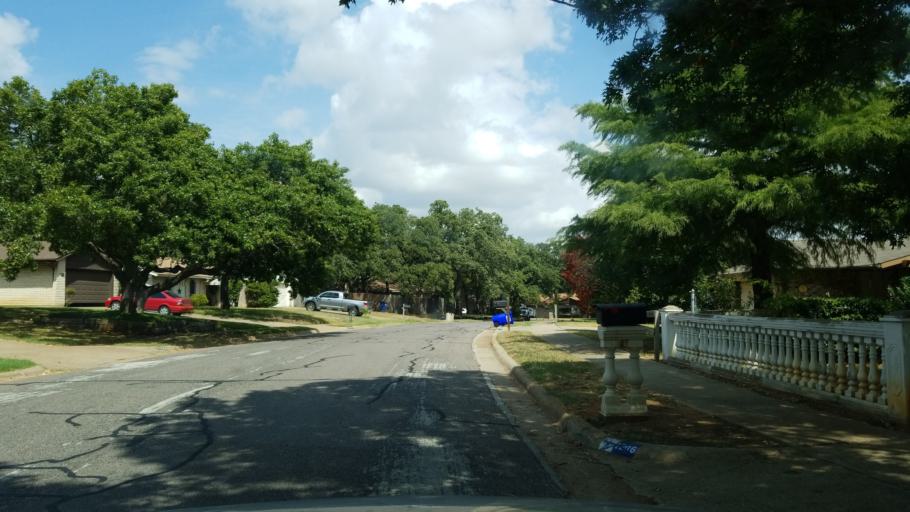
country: US
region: Texas
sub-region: Tarrant County
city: Euless
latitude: 32.8541
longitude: -97.0876
